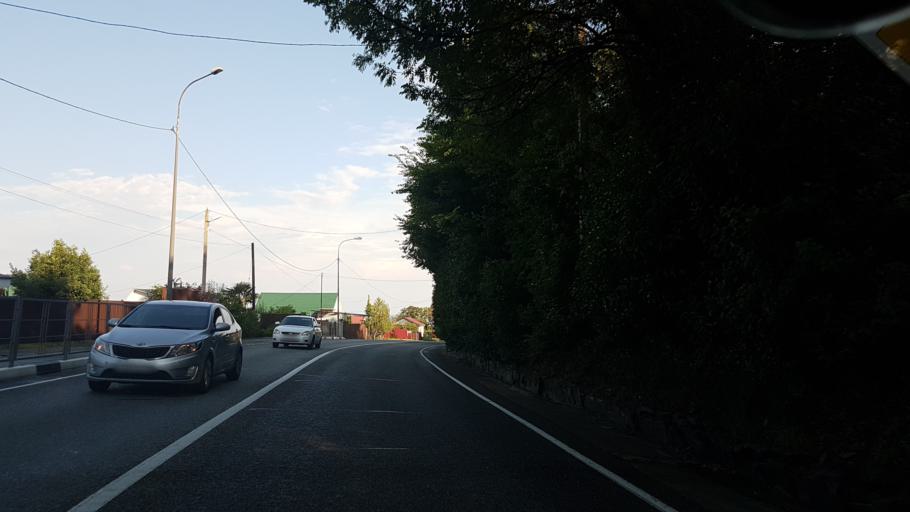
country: RU
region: Krasnodarskiy
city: Vardane
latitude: 43.7623
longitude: 39.5048
